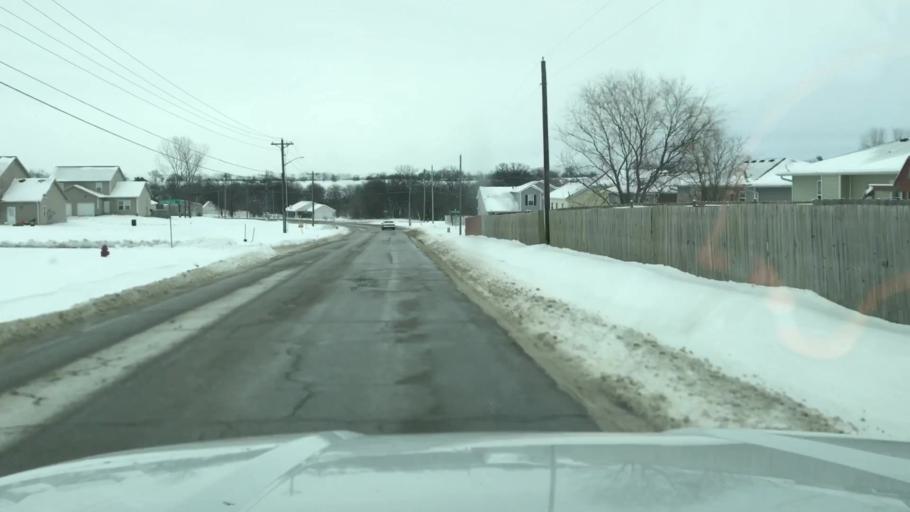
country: US
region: Missouri
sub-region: Clinton County
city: Cameron
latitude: 39.7424
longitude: -94.2178
